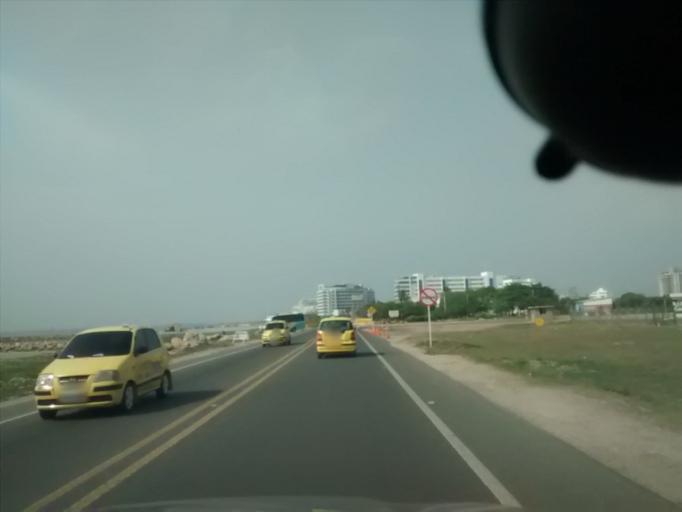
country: CO
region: Bolivar
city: Cartagena
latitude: 10.4545
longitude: -75.5126
